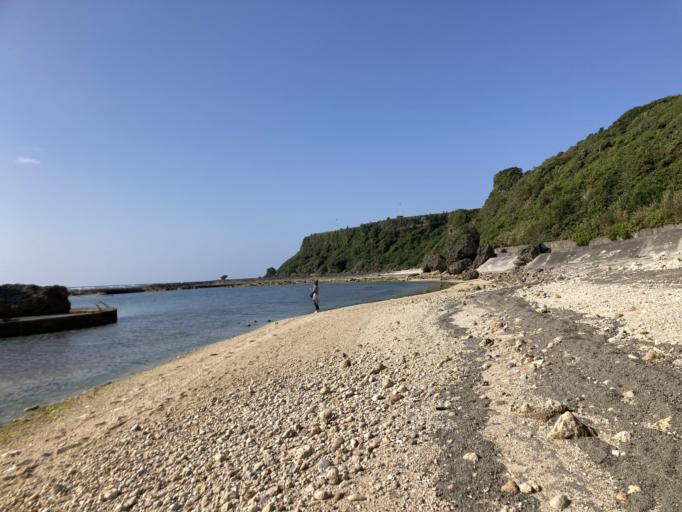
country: JP
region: Okinawa
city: Itoman
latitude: 26.1163
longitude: 127.7453
